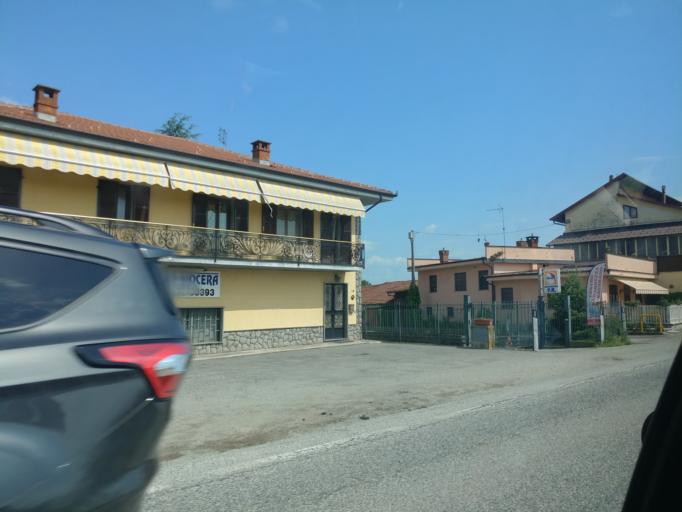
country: IT
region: Piedmont
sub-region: Provincia di Torino
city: Cavour
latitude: 44.7488
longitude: 7.4081
